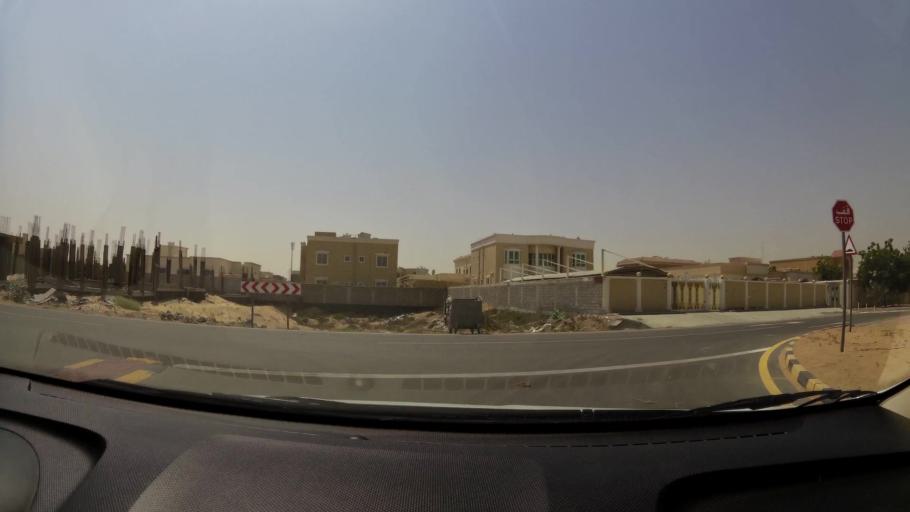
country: AE
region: Ajman
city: Ajman
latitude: 25.4232
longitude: 55.5207
